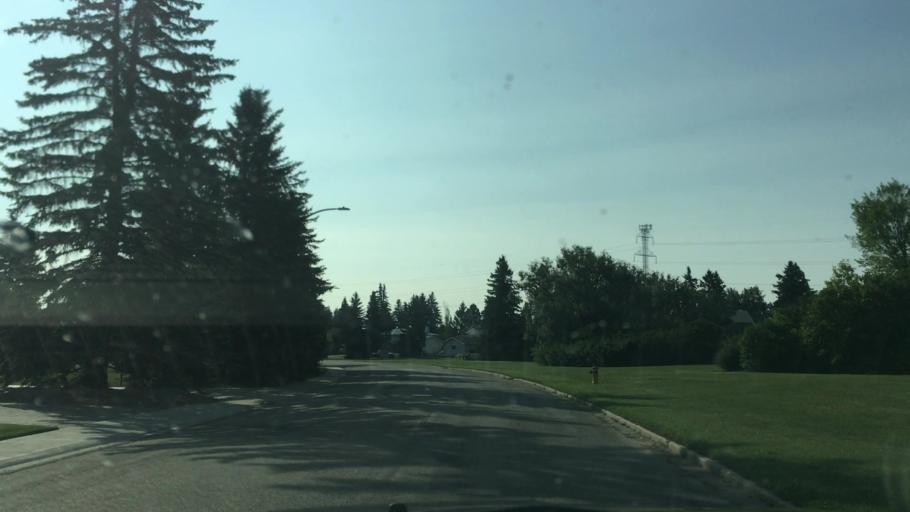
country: CA
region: Alberta
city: Edmonton
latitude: 53.4635
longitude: -113.5445
